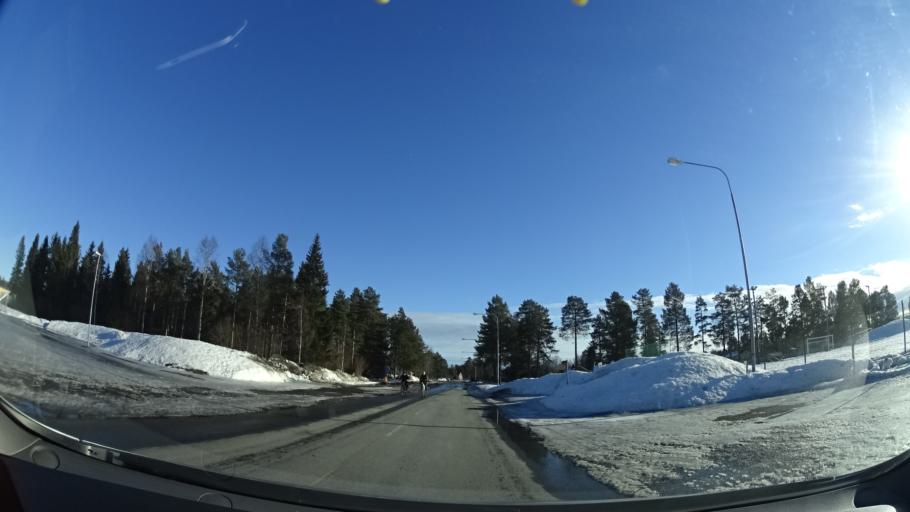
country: SE
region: Vaesterbotten
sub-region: Skelleftea Kommun
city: Byske
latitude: 64.9553
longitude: 21.2116
